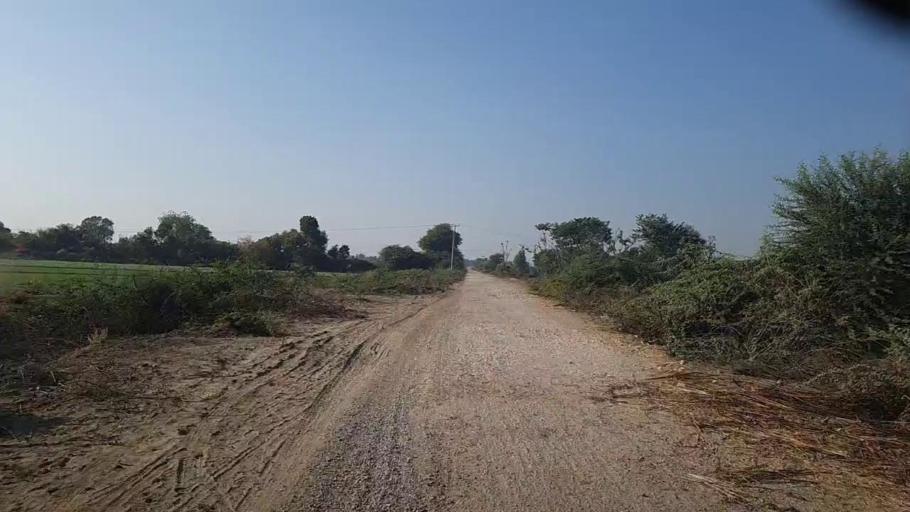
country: PK
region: Sindh
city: Darya Khan Marri
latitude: 26.6750
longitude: 68.3782
